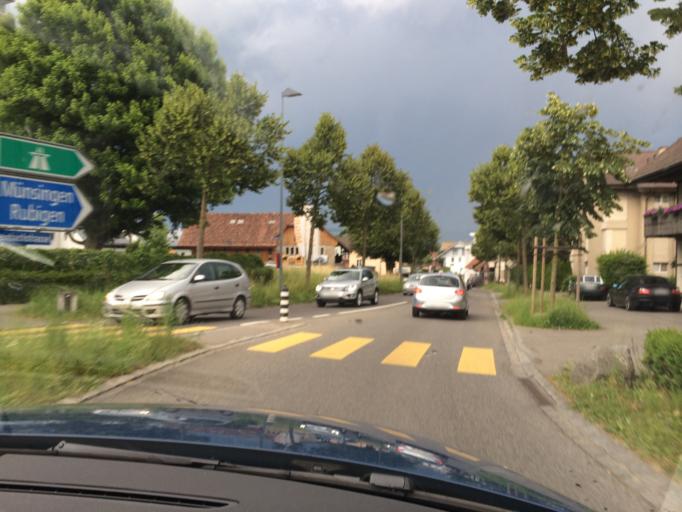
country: CH
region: Bern
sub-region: Bern-Mittelland District
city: Belp
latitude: 46.8953
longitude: 7.4951
